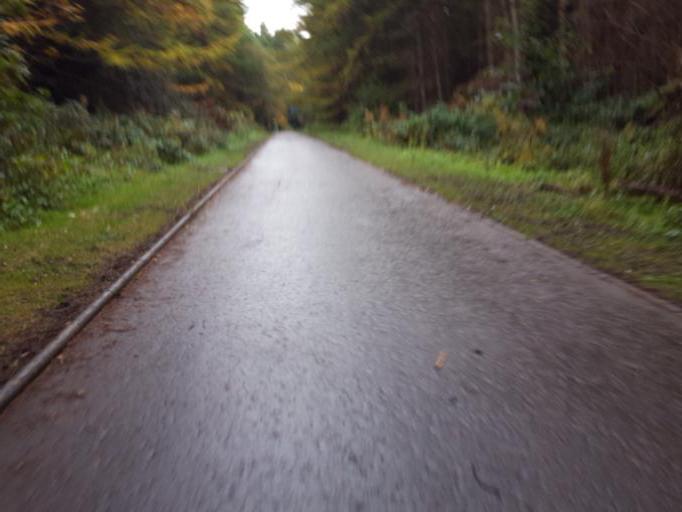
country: GB
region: Scotland
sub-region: West Lothian
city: Livingston
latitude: 55.8915
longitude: -3.5541
